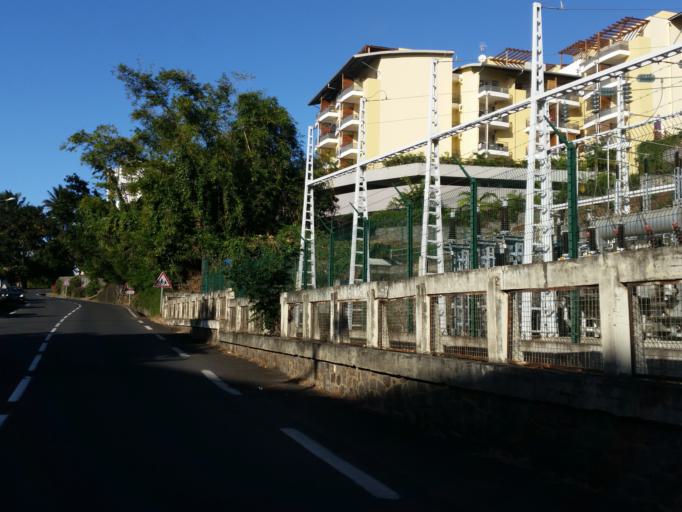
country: RE
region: Reunion
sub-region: Reunion
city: Saint-Denis
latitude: -20.8993
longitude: 55.4601
